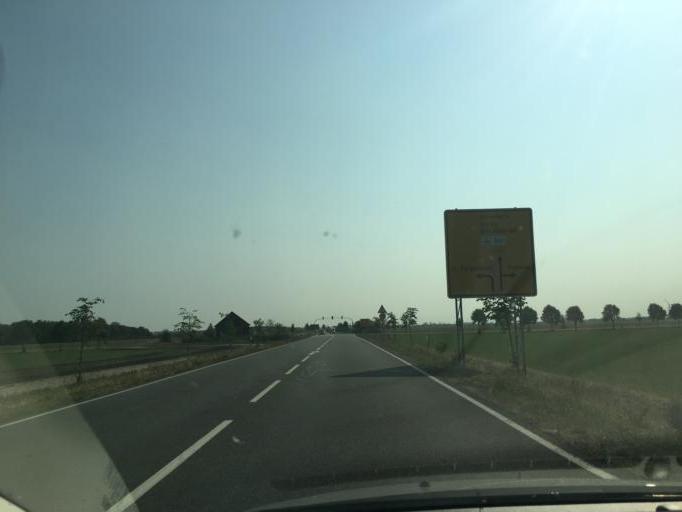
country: DE
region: Saxony-Anhalt
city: Schonebeck
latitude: 51.9895
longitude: 11.7564
